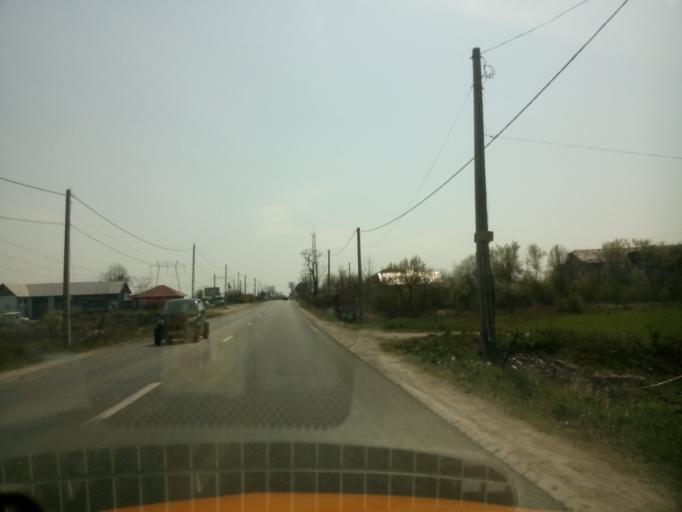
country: RO
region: Calarasi
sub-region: Comuna Frumusani
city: Frumusani
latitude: 44.3171
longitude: 26.2759
